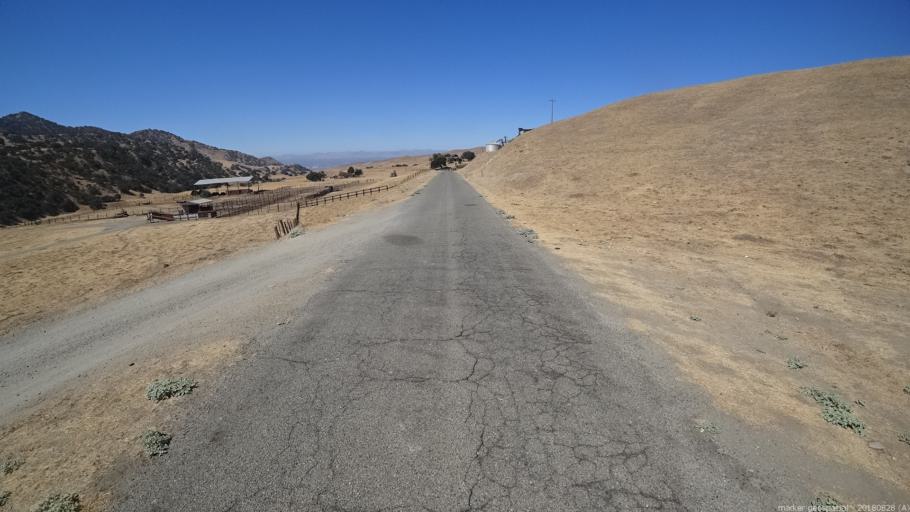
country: US
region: California
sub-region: San Luis Obispo County
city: San Miguel
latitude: 36.0670
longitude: -120.7800
